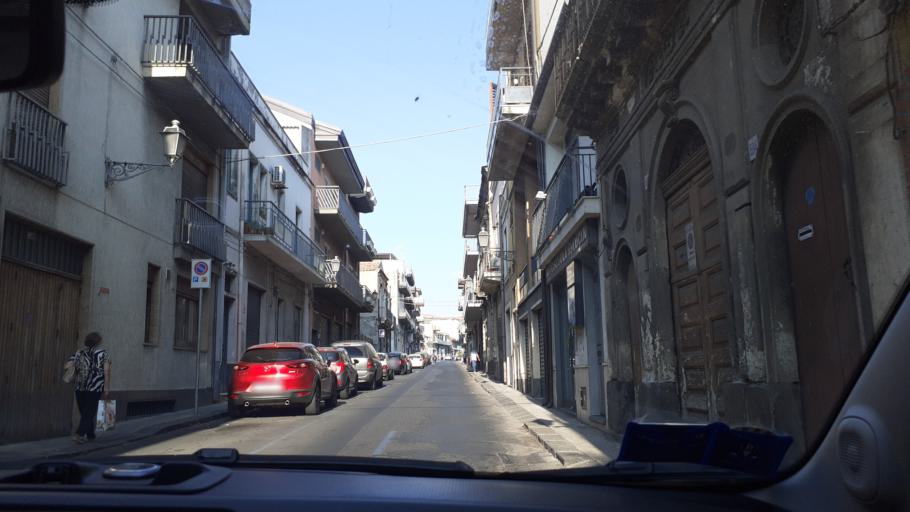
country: IT
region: Sicily
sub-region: Catania
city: Belvedere-Piano Tavola
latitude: 37.5185
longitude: 15.0050
